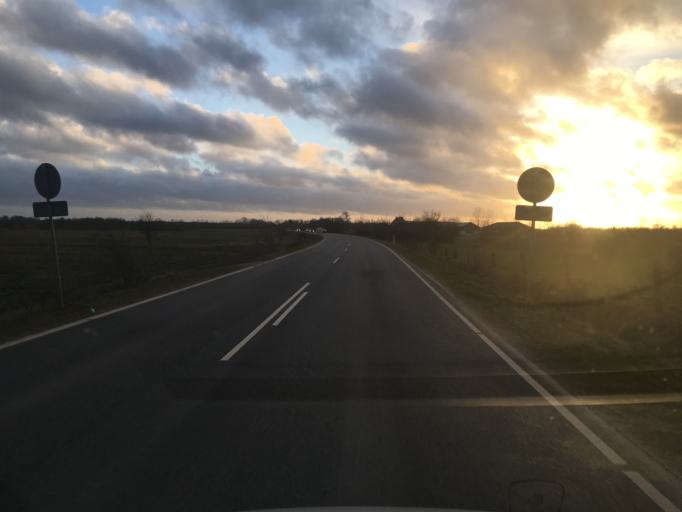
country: DK
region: South Denmark
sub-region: Aabenraa Kommune
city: Tinglev
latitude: 54.9631
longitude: 9.2972
